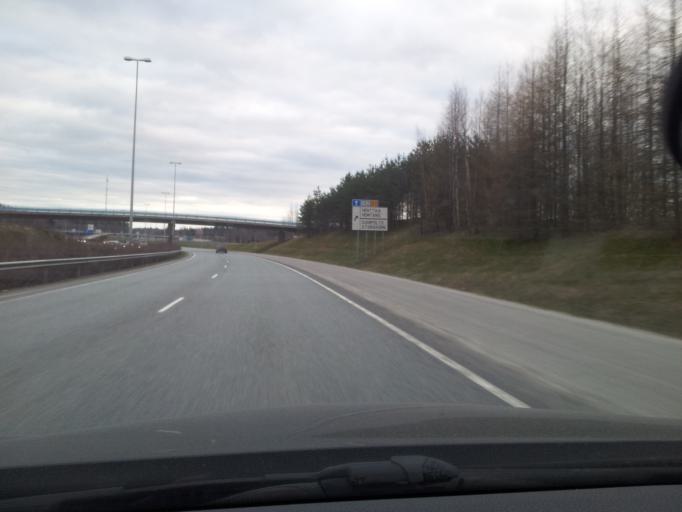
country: FI
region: Uusimaa
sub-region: Helsinki
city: Kauniainen
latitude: 60.1944
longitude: 24.7432
